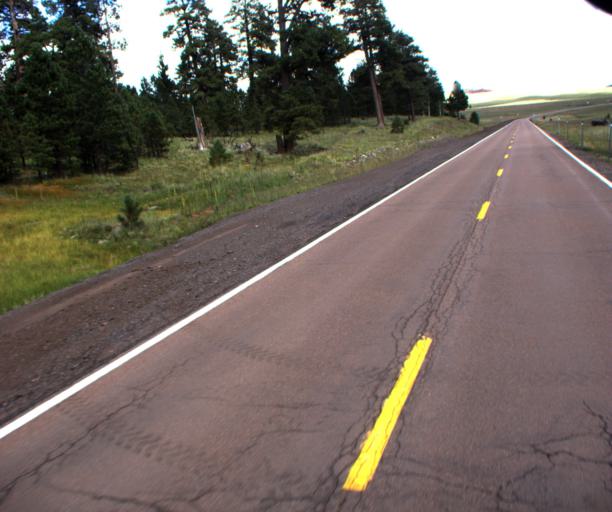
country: US
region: Arizona
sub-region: Apache County
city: Eagar
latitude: 34.0544
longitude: -109.5542
